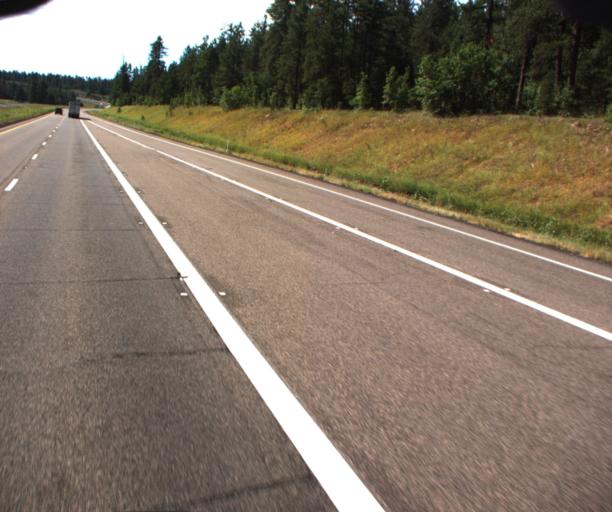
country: US
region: Arizona
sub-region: Coconino County
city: Sedona
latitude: 34.8723
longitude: -111.6330
